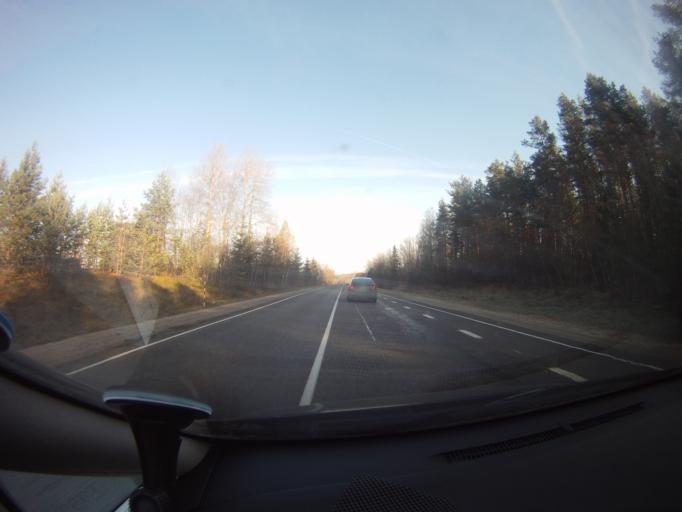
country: BY
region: Minsk
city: Syomkava
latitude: 54.1772
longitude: 27.5000
